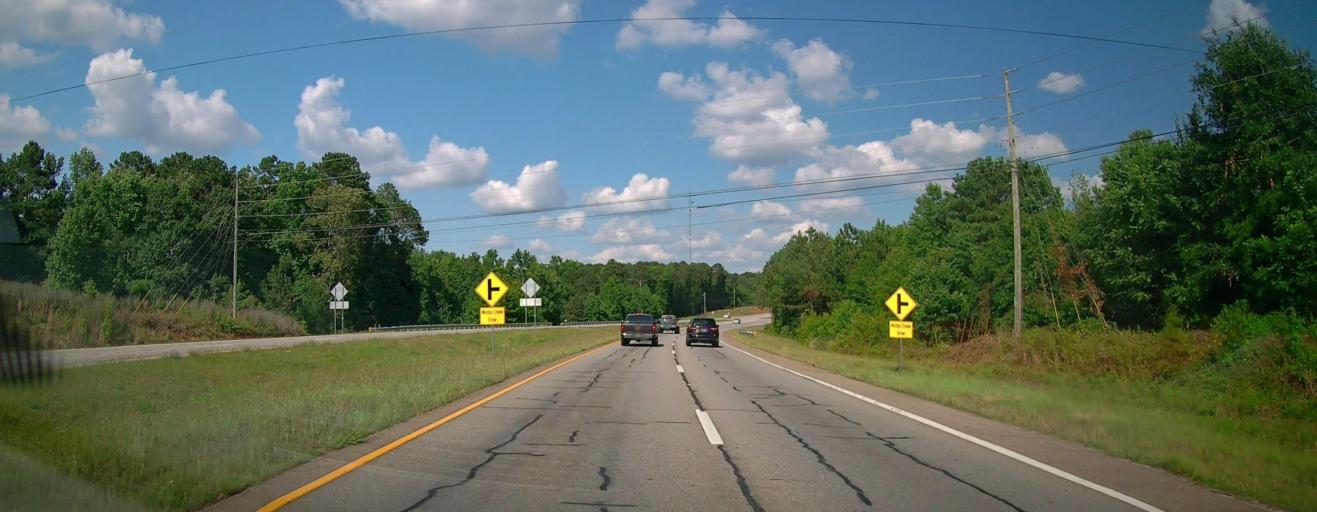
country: US
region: Georgia
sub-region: Henry County
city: Hampton
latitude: 33.4016
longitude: -84.2347
